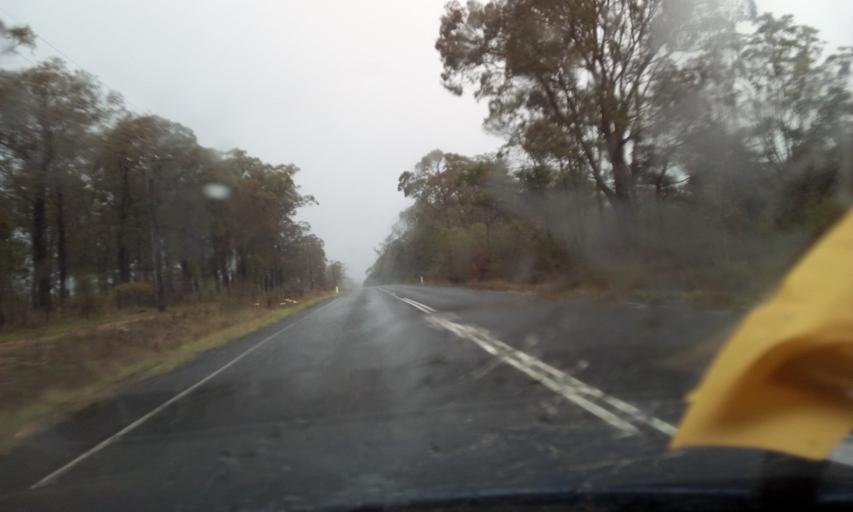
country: AU
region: New South Wales
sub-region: Wollondilly
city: Douglas Park
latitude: -34.2205
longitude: 150.7246
